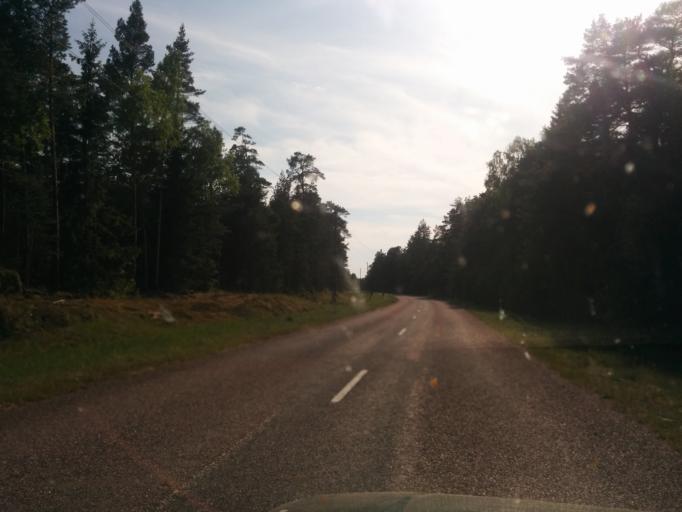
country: LV
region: Dundaga
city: Dundaga
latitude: 57.6697
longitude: 22.3179
